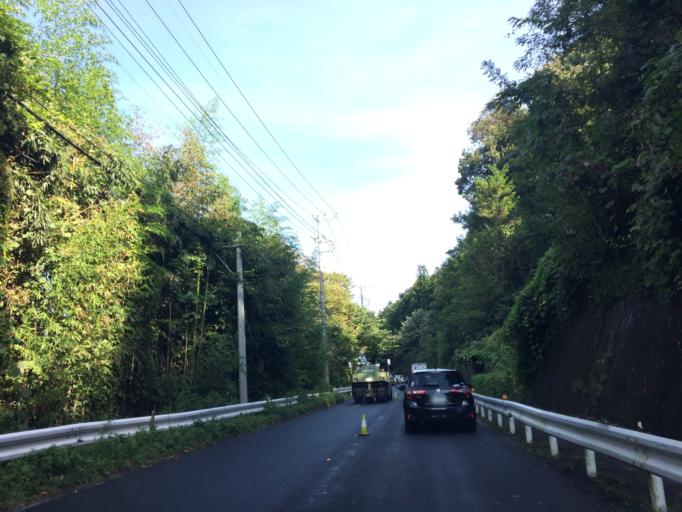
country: JP
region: Gunma
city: Nakanojomachi
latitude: 36.5494
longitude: 138.9121
